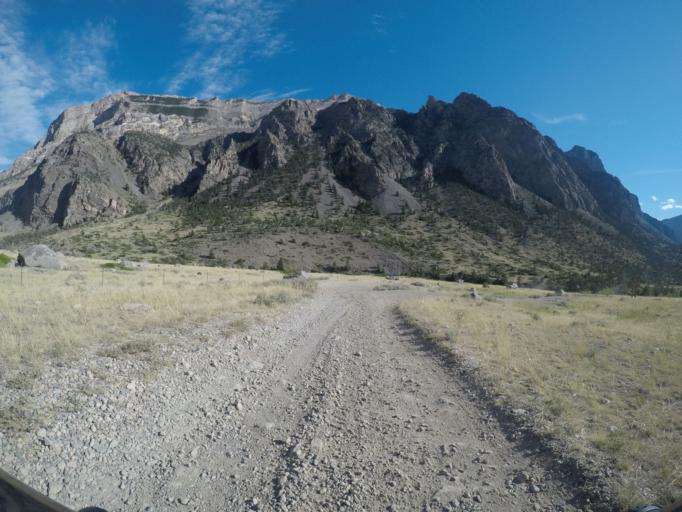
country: US
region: Montana
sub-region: Carbon County
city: Red Lodge
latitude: 44.8433
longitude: -109.3169
